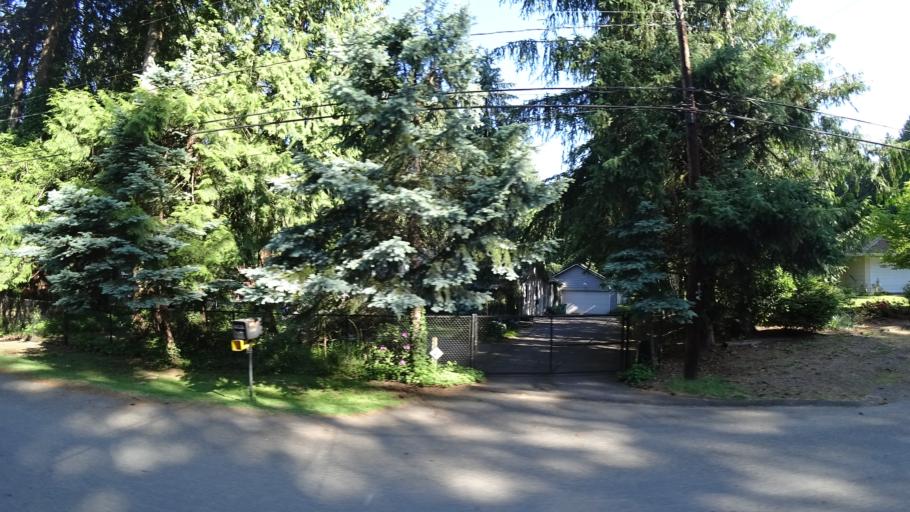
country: US
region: Oregon
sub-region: Clackamas County
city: Happy Valley
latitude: 45.4728
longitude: -122.5398
